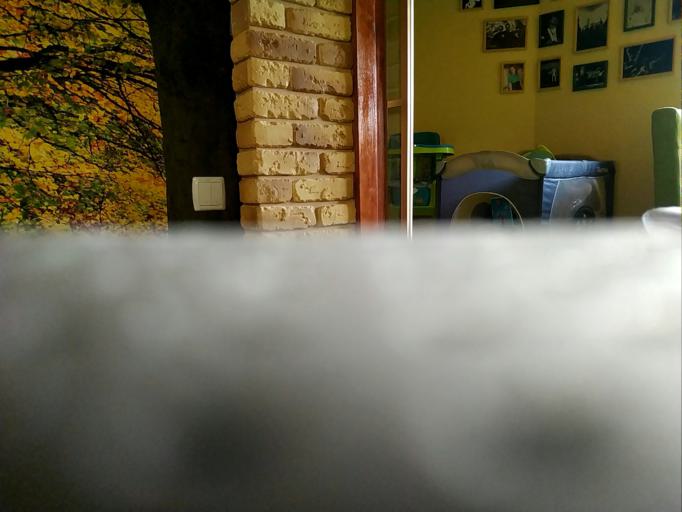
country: RU
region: Kaluga
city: Seredeyskiy
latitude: 53.9674
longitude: 35.3298
